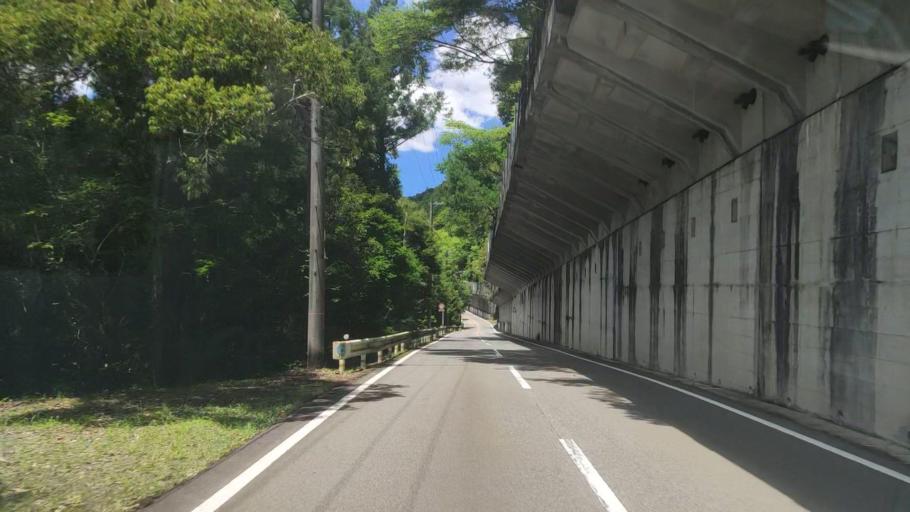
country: JP
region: Mie
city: Owase
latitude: 33.9982
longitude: 136.0117
